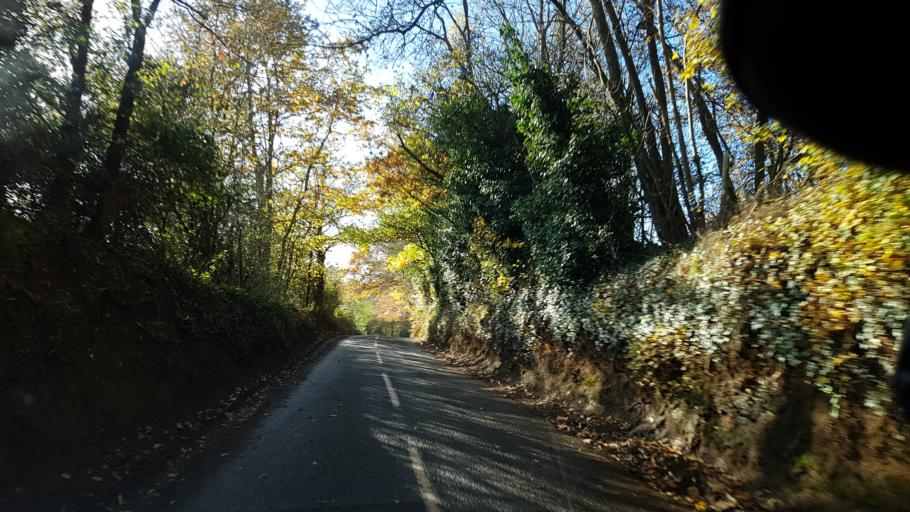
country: GB
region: England
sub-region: Surrey
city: Elstead
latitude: 51.2128
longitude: -0.6762
